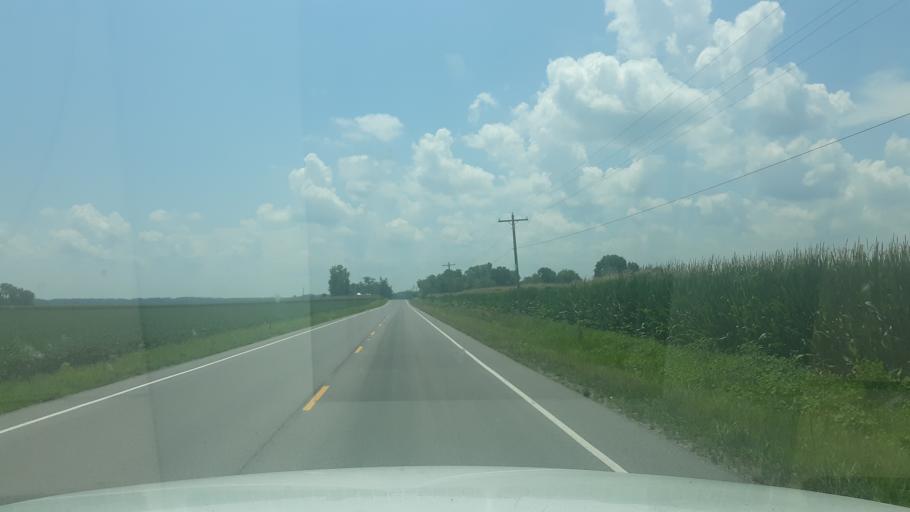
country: US
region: Illinois
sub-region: Saline County
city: Harrisburg
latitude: 37.8047
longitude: -88.5398
